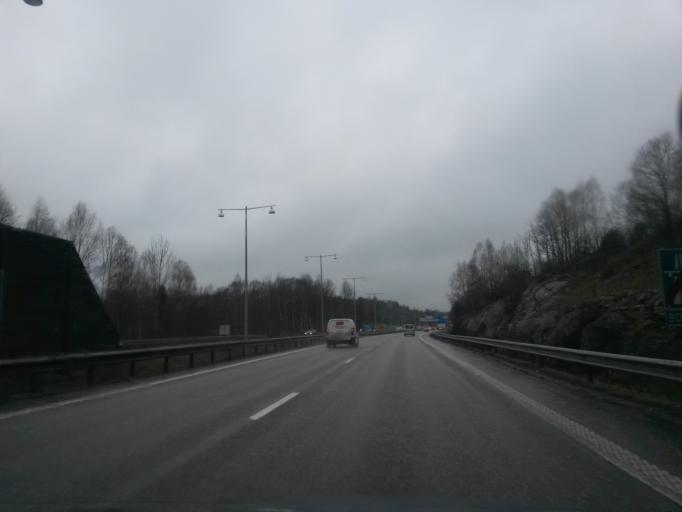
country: SE
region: Vaestra Goetaland
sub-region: Uddevalla Kommun
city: Uddevalla
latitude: 58.3520
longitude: 11.8761
